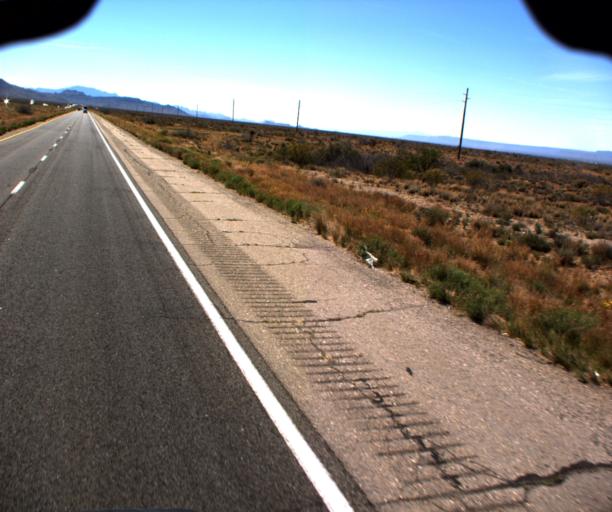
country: US
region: Arizona
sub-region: Mohave County
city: Golden Valley
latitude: 35.3147
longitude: -114.2001
